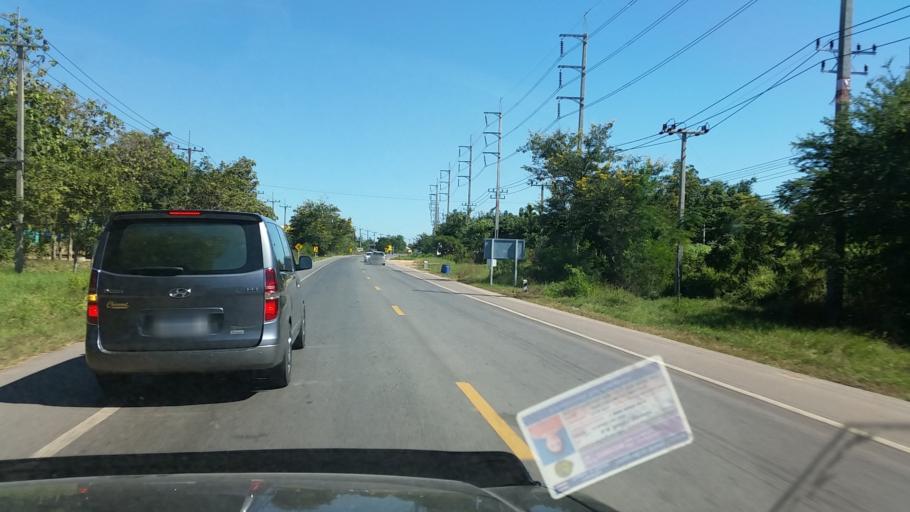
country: TH
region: Chaiyaphum
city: Ban Khwao
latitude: 15.7852
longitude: 101.9565
